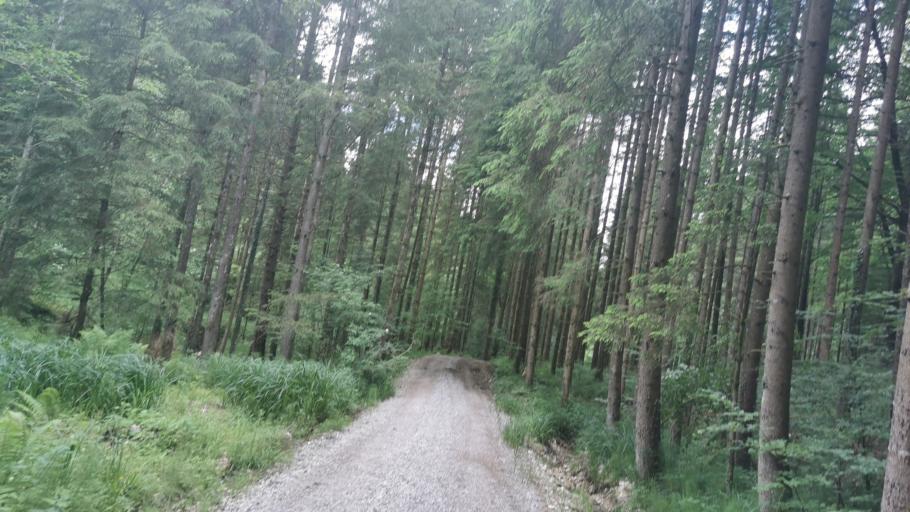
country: AT
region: Salzburg
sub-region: Politischer Bezirk Salzburg-Umgebung
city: Grodig
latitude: 47.7502
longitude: 12.9781
